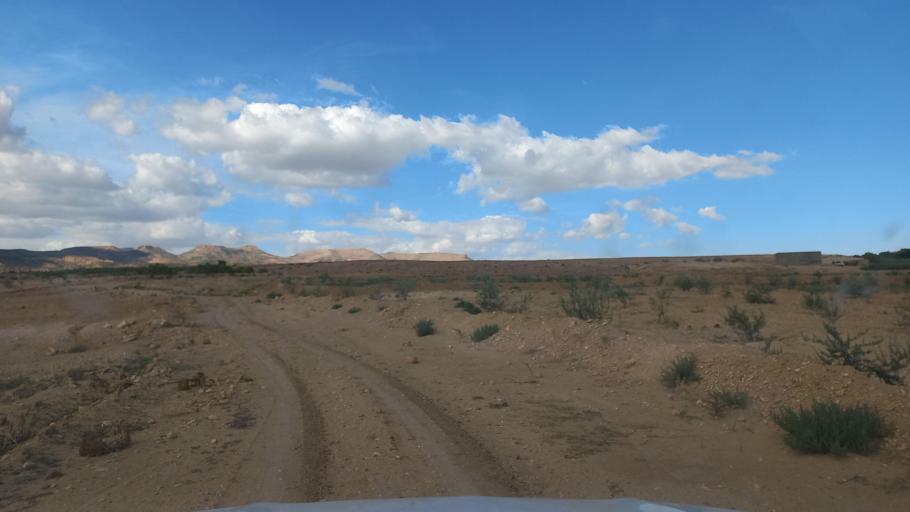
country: TN
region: Al Qasrayn
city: Sbiba
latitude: 35.4012
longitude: 9.0110
